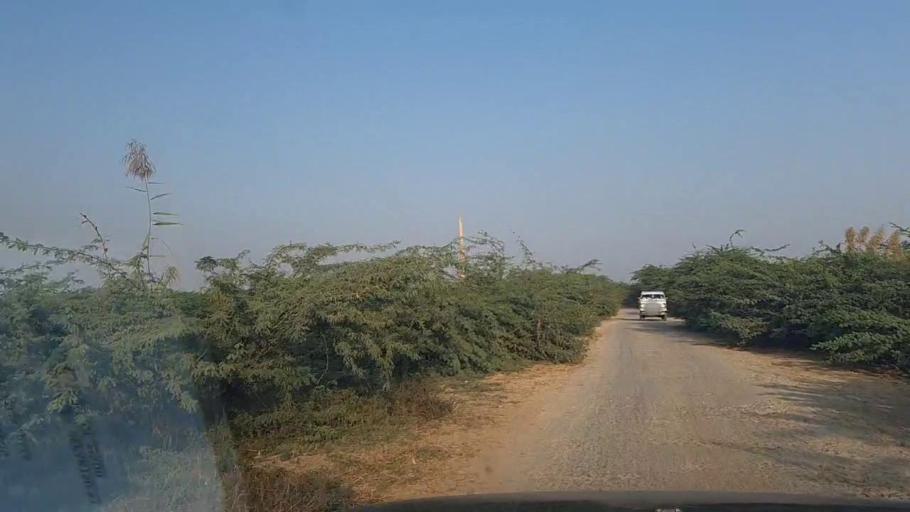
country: PK
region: Sindh
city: Keti Bandar
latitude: 24.2660
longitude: 67.5667
